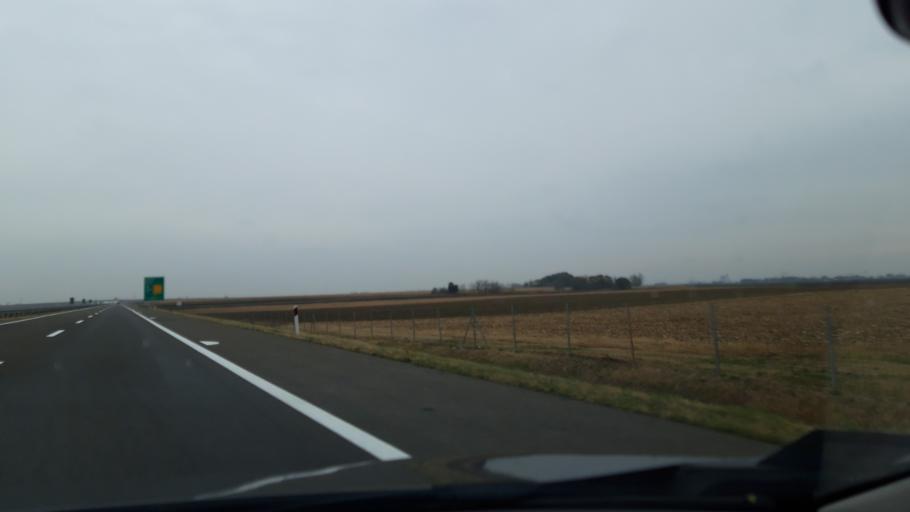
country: RS
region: Autonomna Pokrajina Vojvodina
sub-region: Severnobacki Okrug
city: Backa Topola
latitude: 45.9216
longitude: 19.7046
